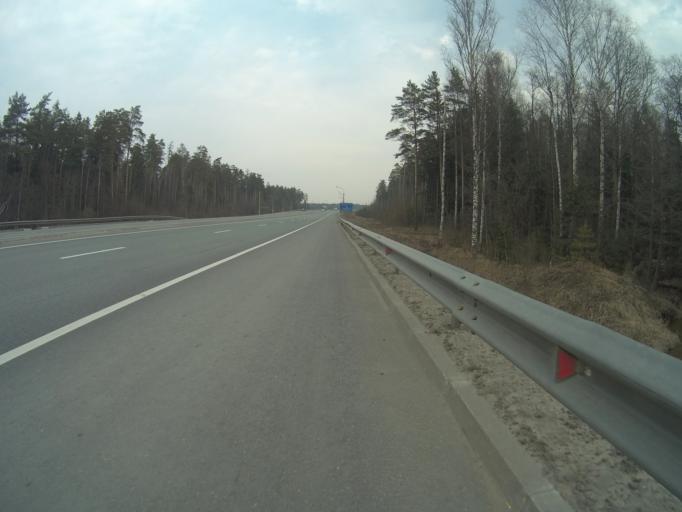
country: RU
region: Vladimir
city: Kommunar
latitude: 56.0729
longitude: 40.4662
